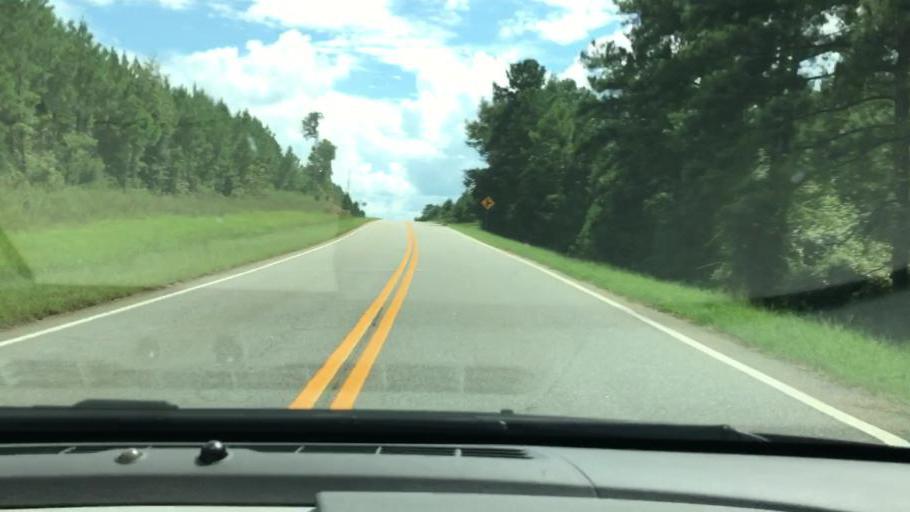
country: US
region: Georgia
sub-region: Quitman County
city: Georgetown
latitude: 31.9219
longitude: -85.0598
